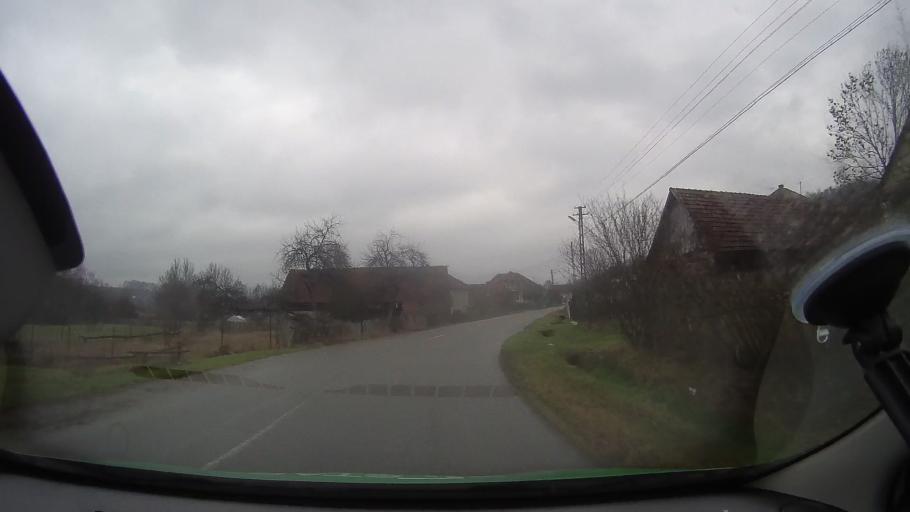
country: RO
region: Hunedoara
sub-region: Comuna Tomesti
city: Tomesti
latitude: 46.2077
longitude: 22.6624
